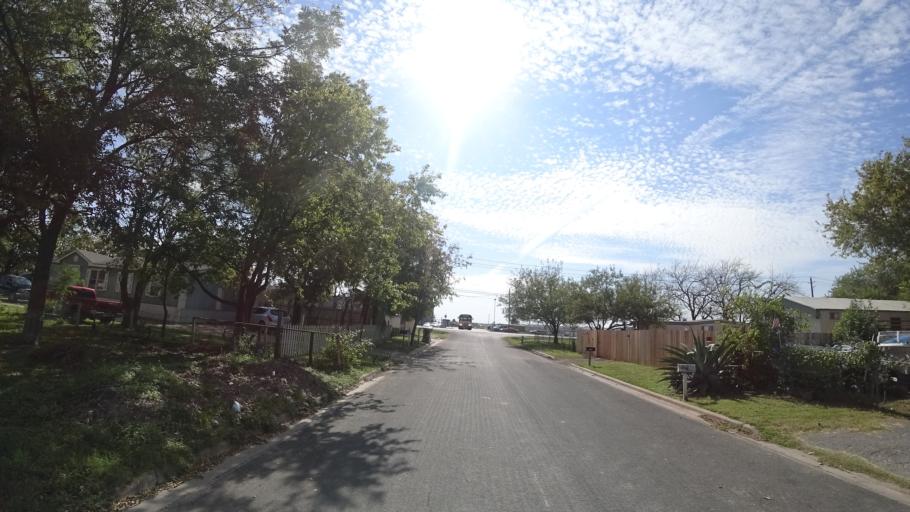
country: US
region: Texas
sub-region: Travis County
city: Pflugerville
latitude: 30.4067
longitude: -97.6294
